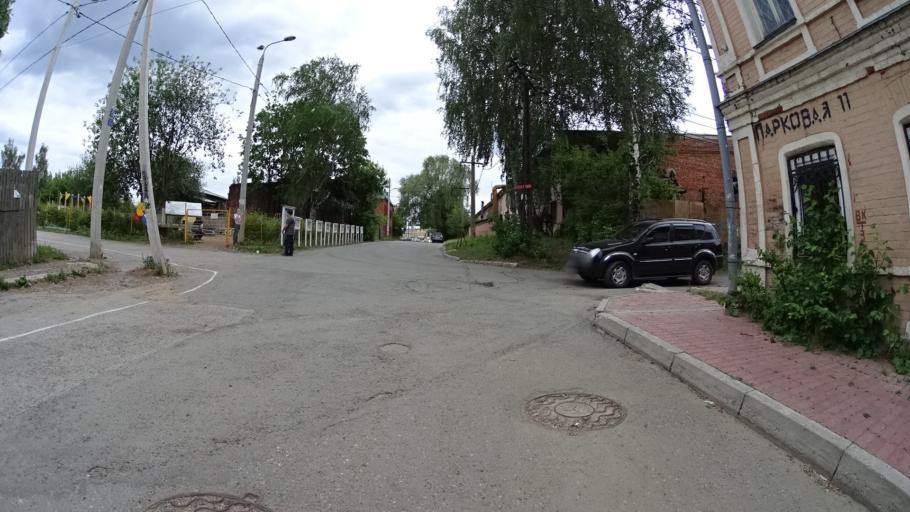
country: RU
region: Perm
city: Perm
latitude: 58.0177
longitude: 56.2644
